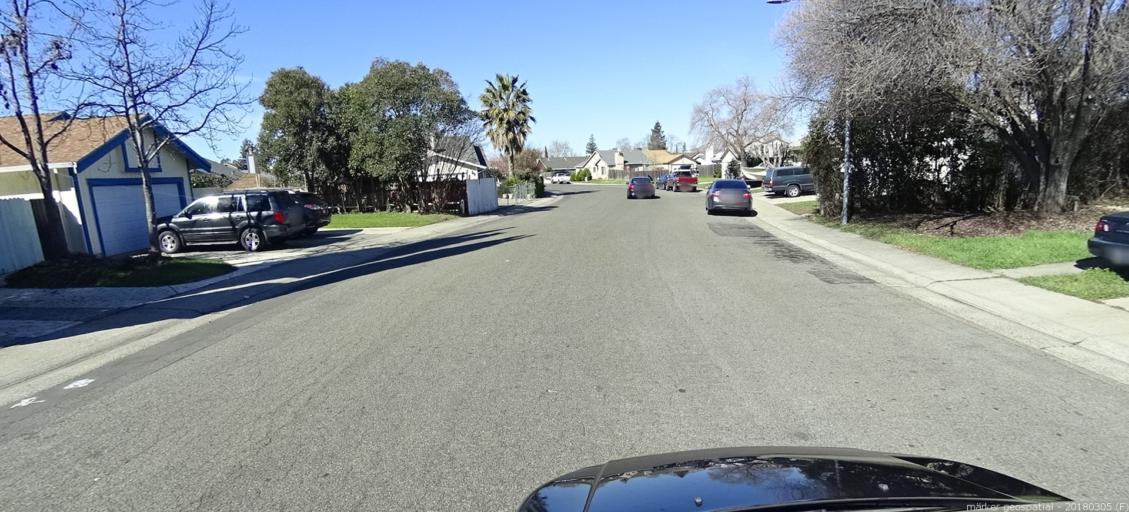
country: US
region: California
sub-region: Sacramento County
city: Florin
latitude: 38.4872
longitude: -121.4167
